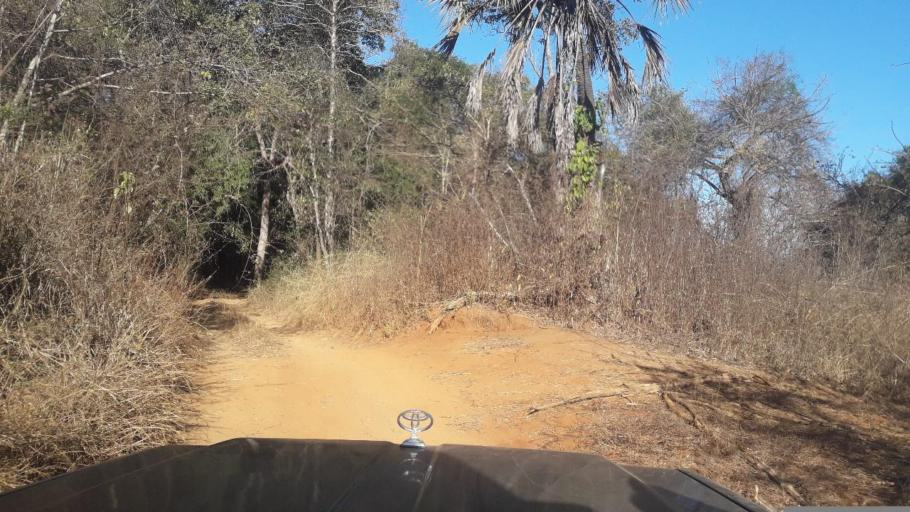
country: MG
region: Boeny
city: Sitampiky
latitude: -16.4185
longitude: 45.6129
